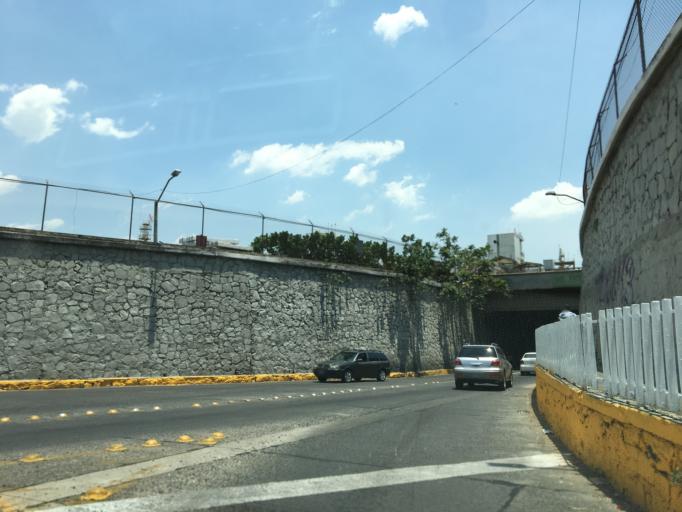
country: MX
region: Jalisco
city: Guadalajara
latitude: 20.6629
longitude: -103.3668
